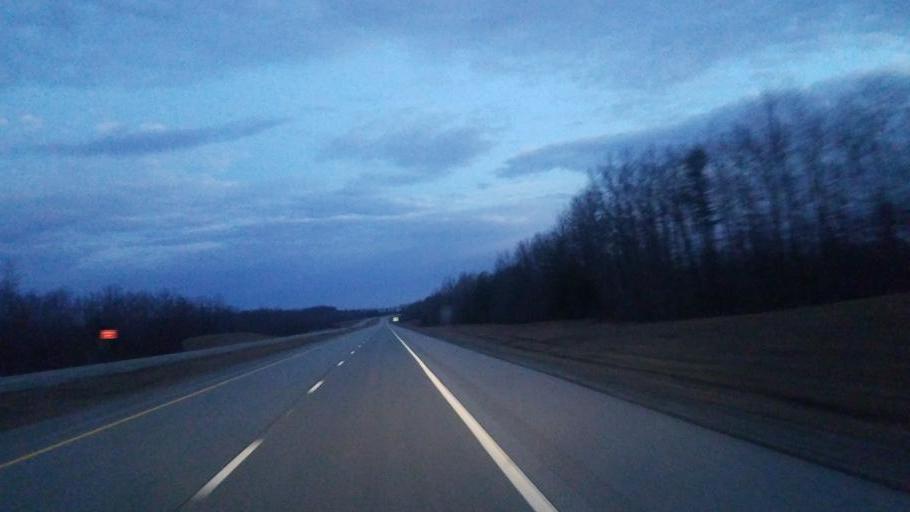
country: US
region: Tennessee
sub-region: Van Buren County
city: Spencer
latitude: 35.6110
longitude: -85.4711
